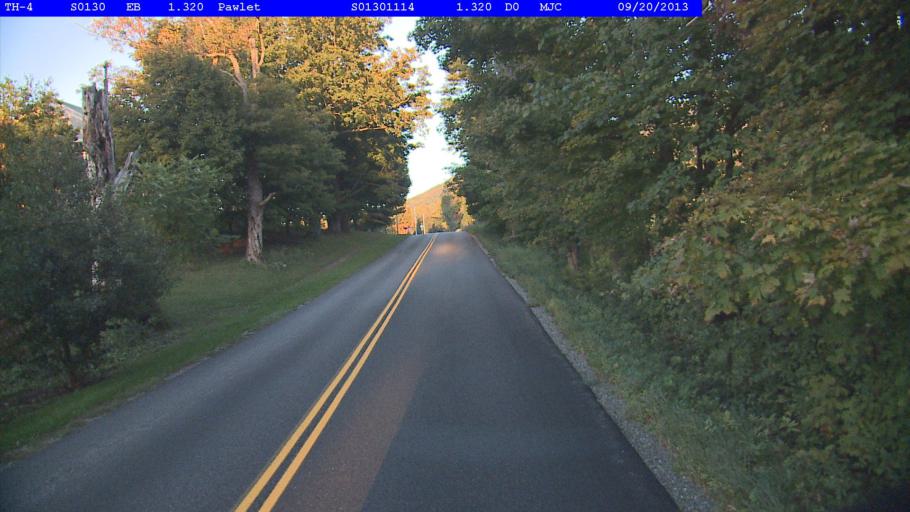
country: US
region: New York
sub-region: Washington County
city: Granville
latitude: 43.3579
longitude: -73.1285
